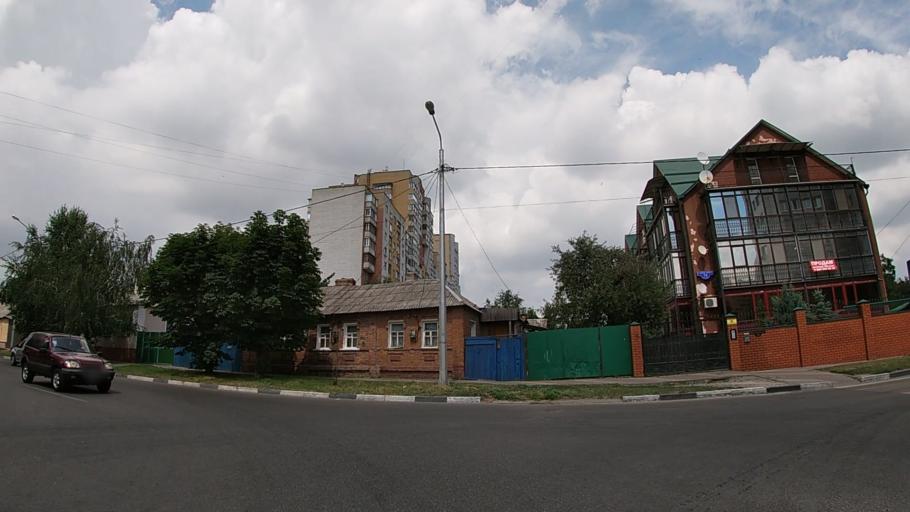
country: RU
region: Belgorod
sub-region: Belgorodskiy Rayon
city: Belgorod
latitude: 50.6059
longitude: 36.5961
